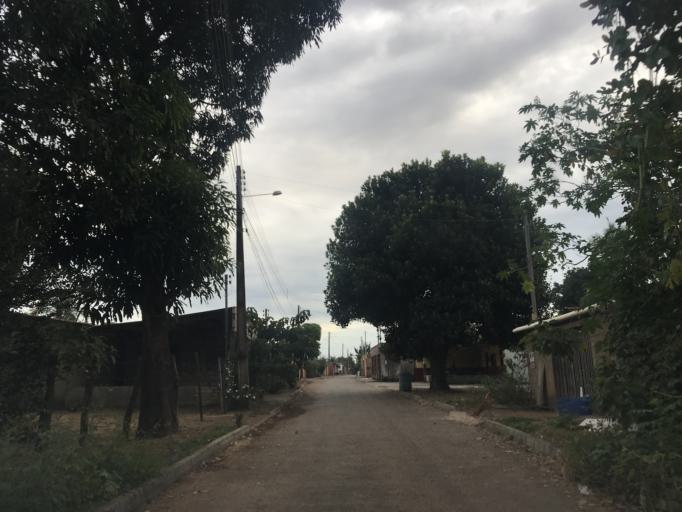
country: BR
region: Goias
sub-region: Padre Bernardo
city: Padre Bernardo
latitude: -15.3607
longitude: -48.2274
